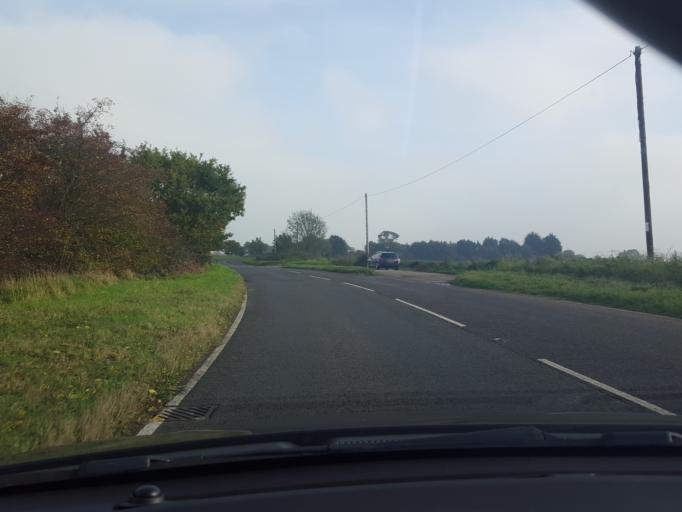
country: GB
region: England
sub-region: Essex
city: Mistley
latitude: 51.9298
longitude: 1.1394
